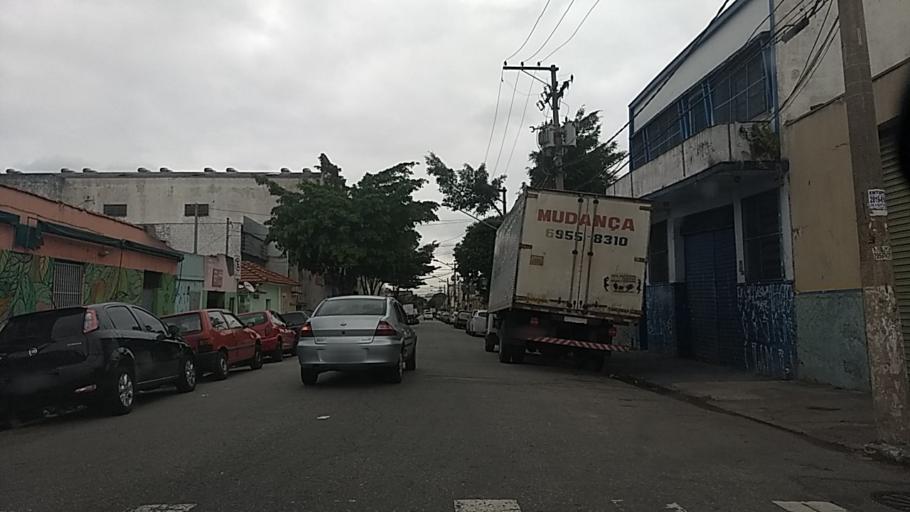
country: BR
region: Sao Paulo
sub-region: Sao Paulo
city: Sao Paulo
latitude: -23.5121
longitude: -46.5890
